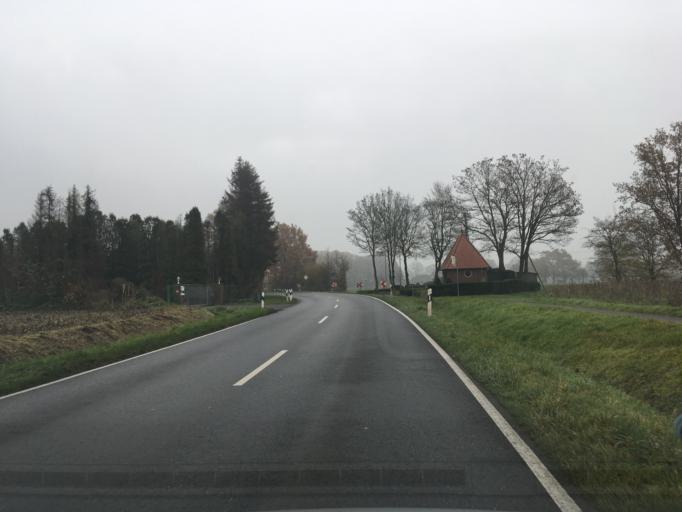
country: DE
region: North Rhine-Westphalia
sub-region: Regierungsbezirk Munster
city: Gescher
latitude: 51.9863
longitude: 6.9689
